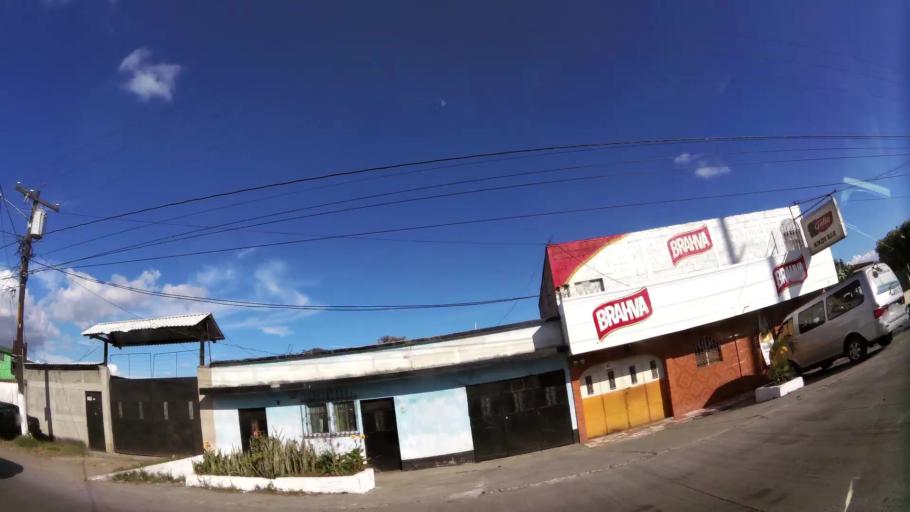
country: GT
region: Guatemala
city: Villa Nueva
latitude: 14.5178
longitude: -90.5737
